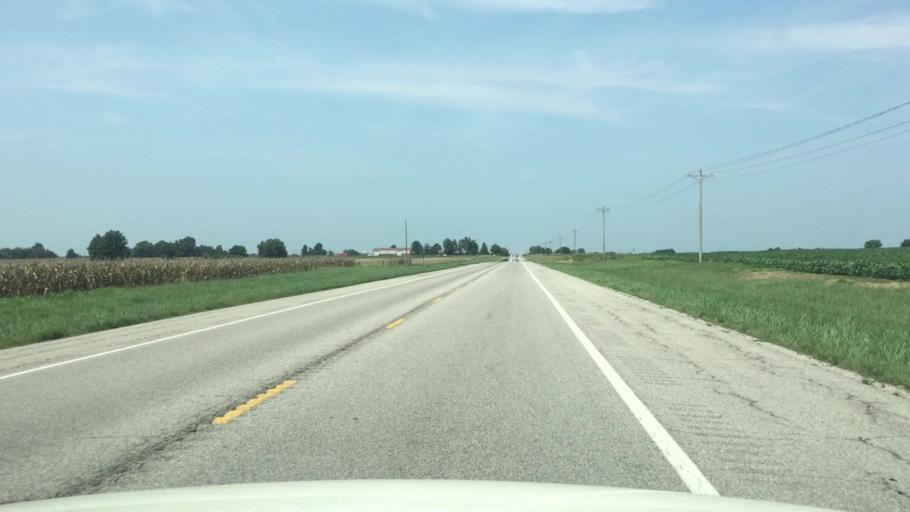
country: US
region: Kansas
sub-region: Crawford County
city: Pittsburg
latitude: 37.2646
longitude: -94.7052
